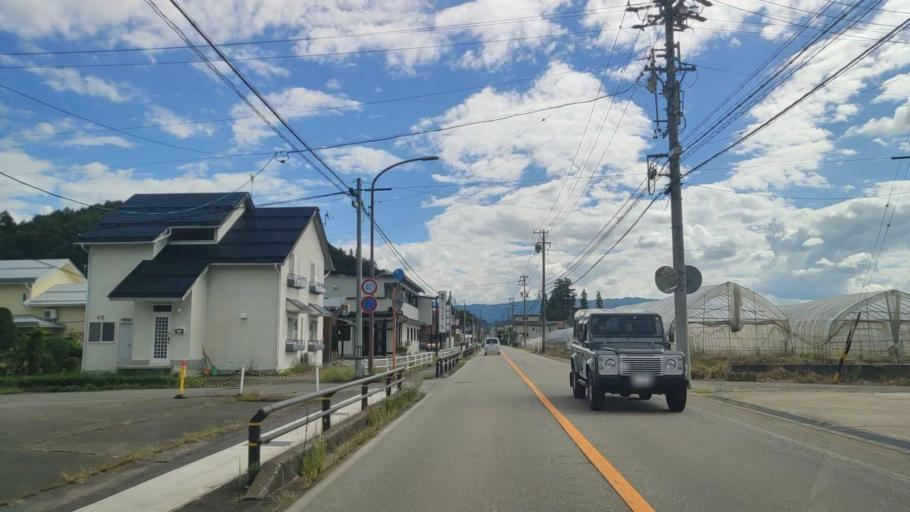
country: JP
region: Gifu
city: Takayama
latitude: 36.1675
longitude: 137.2479
